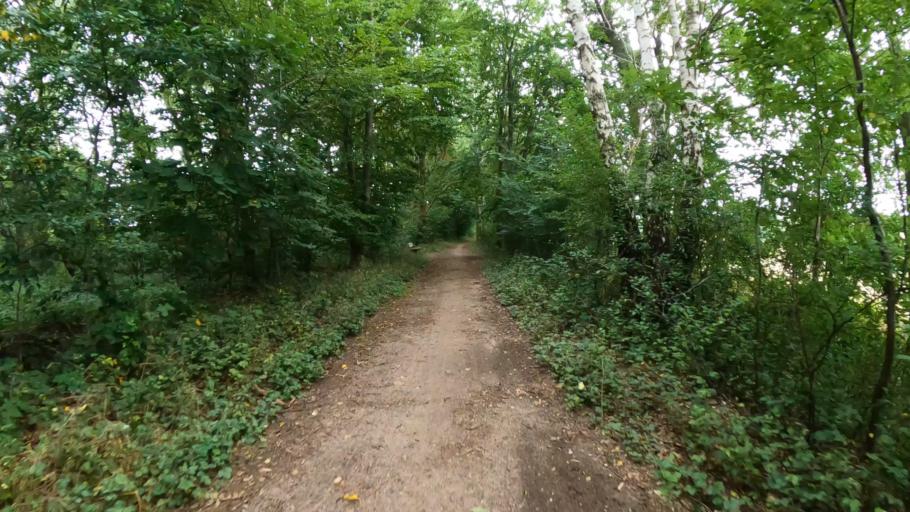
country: DE
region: Lower Saxony
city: Buchholz in der Nordheide
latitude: 53.3181
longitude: 9.8193
